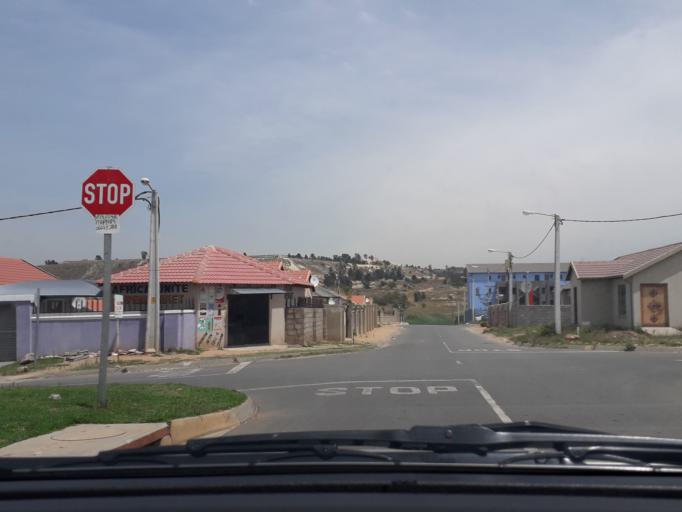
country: ZA
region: Gauteng
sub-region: City of Johannesburg Metropolitan Municipality
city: Roodepoort
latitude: -26.2042
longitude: 27.9105
